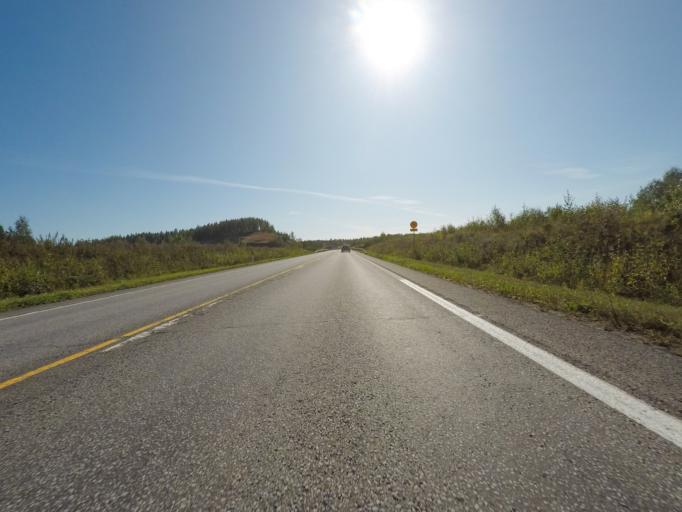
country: FI
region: Southern Savonia
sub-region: Pieksaemaeki
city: Joroinen
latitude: 62.2026
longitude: 27.8619
